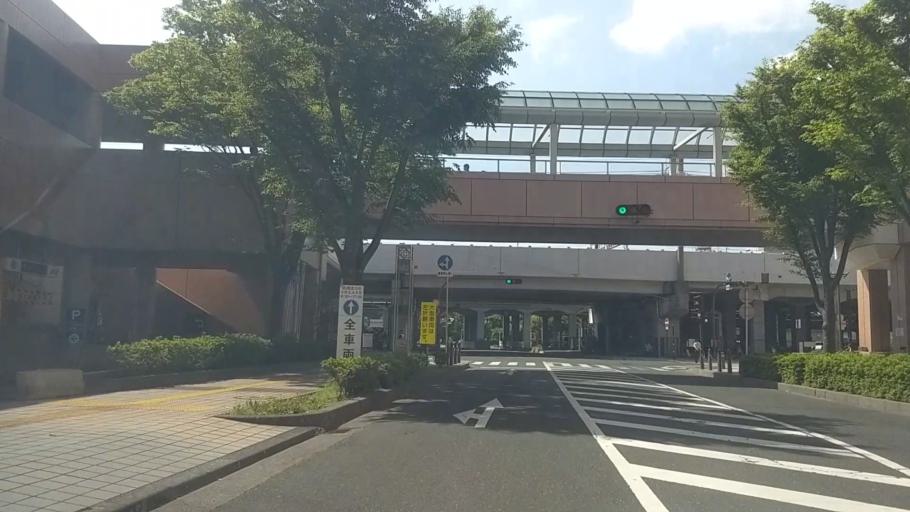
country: JP
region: Shizuoka
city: Hamamatsu
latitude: 34.7058
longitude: 137.7379
